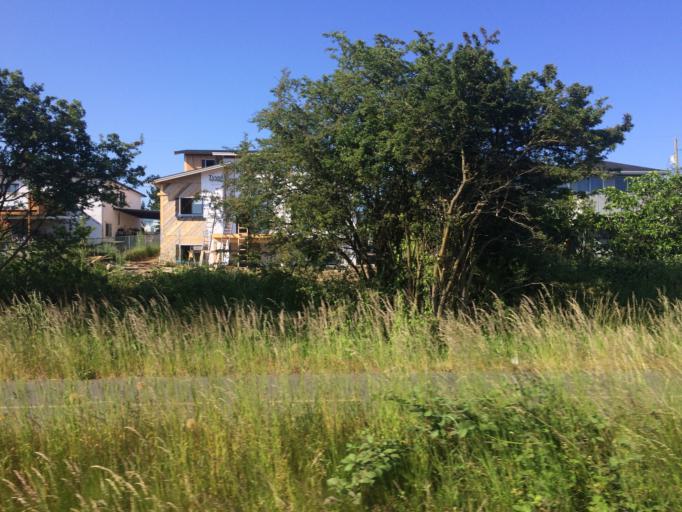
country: CA
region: British Columbia
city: Victoria
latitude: 48.4579
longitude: -123.3888
